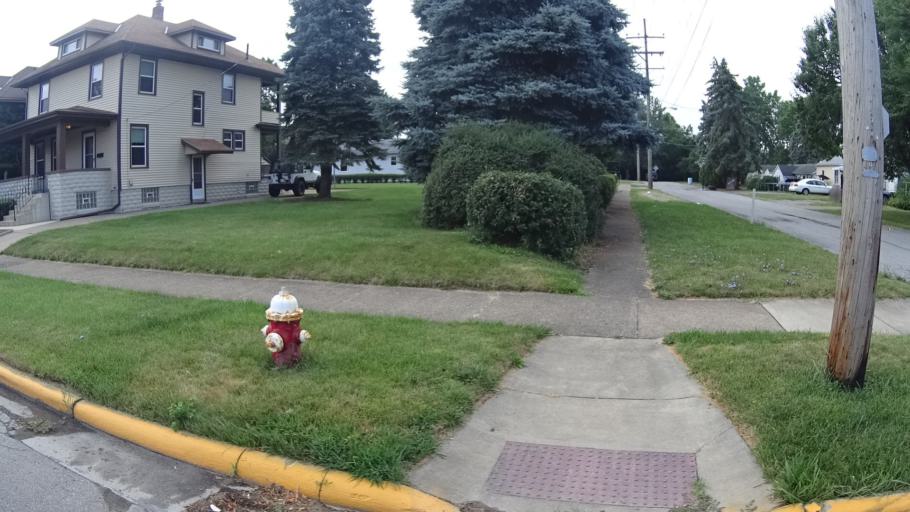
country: US
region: Ohio
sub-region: Erie County
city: Sandusky
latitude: 41.4463
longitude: -82.7326
